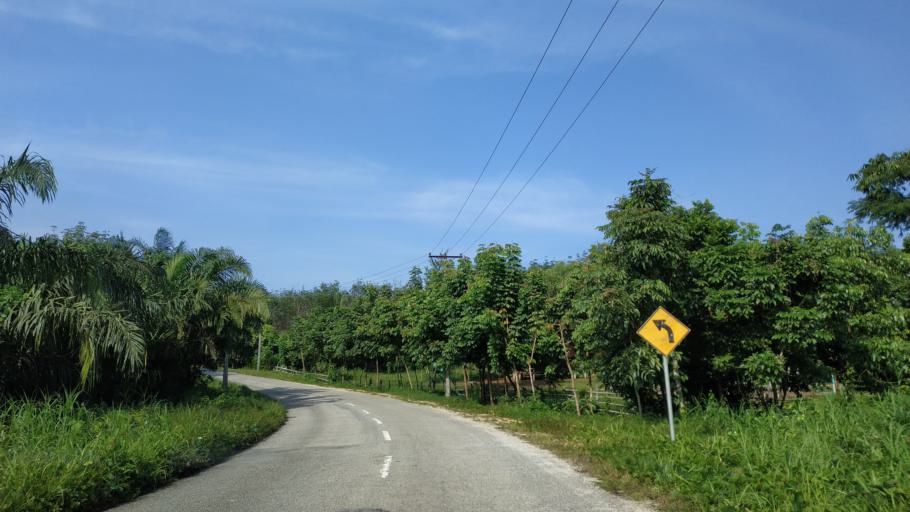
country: MM
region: Tanintharyi
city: Dawei
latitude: 14.5957
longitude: 98.0739
